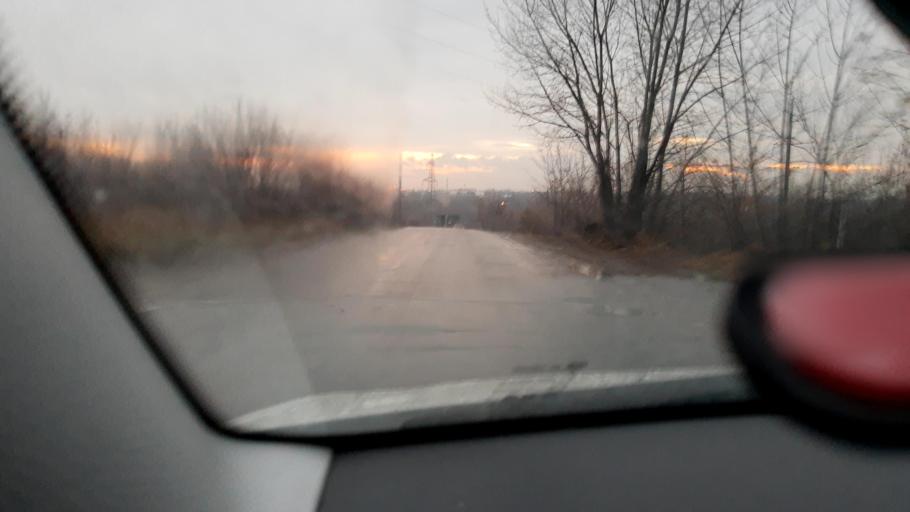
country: RU
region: Bashkortostan
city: Ufa
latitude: 54.8684
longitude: 56.1311
